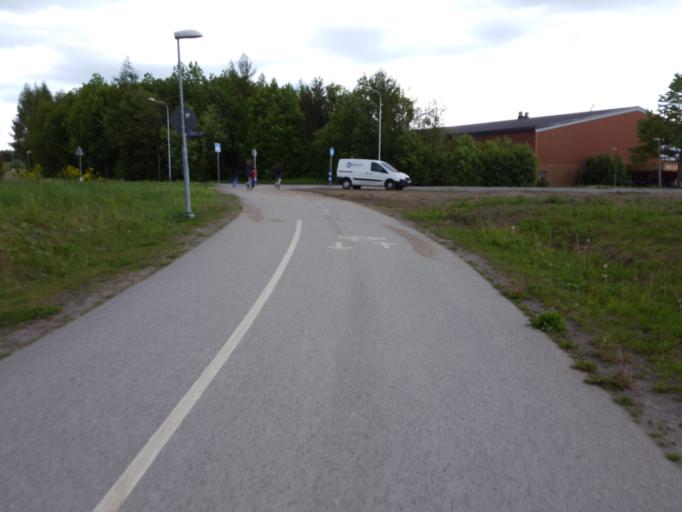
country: SE
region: Uppsala
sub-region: Uppsala Kommun
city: Gamla Uppsala
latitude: 59.8842
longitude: 17.6611
